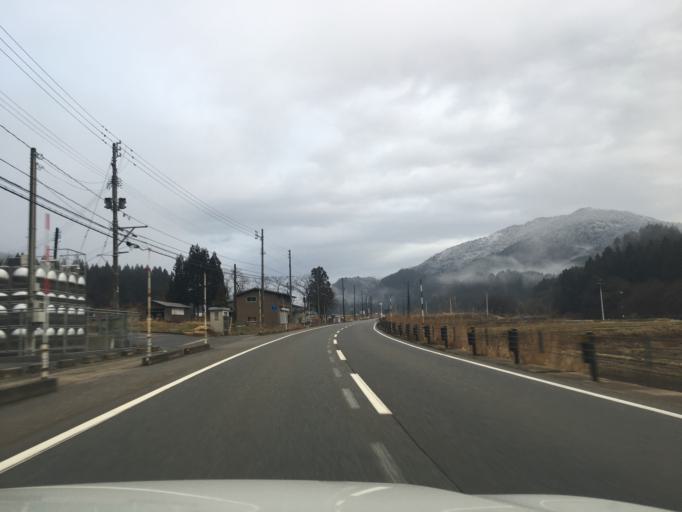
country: JP
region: Niigata
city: Murakami
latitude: 38.3535
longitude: 139.5504
